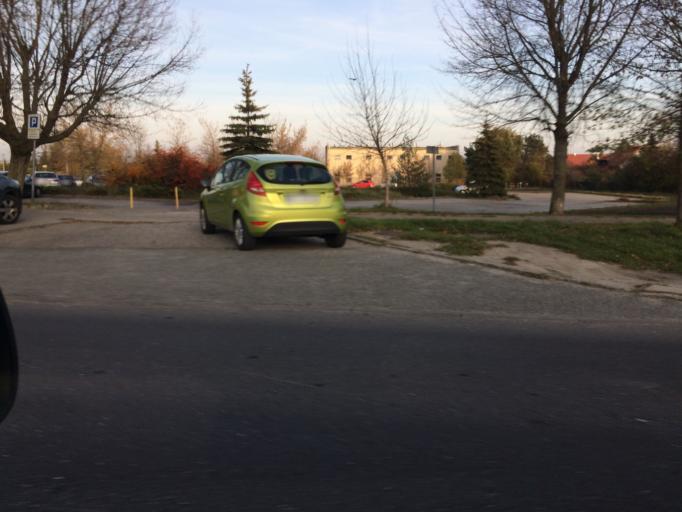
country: PL
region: Opole Voivodeship
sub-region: Powiat opolski
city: Opole
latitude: 50.6748
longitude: 17.9750
